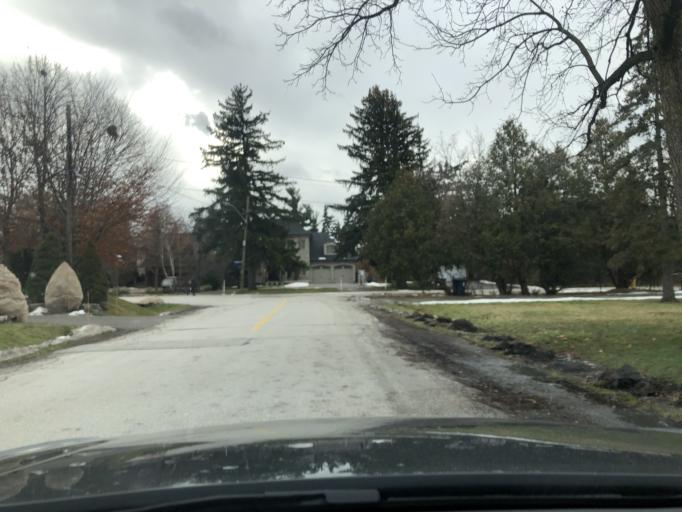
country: CA
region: Ontario
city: Etobicoke
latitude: 43.6951
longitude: -79.5293
